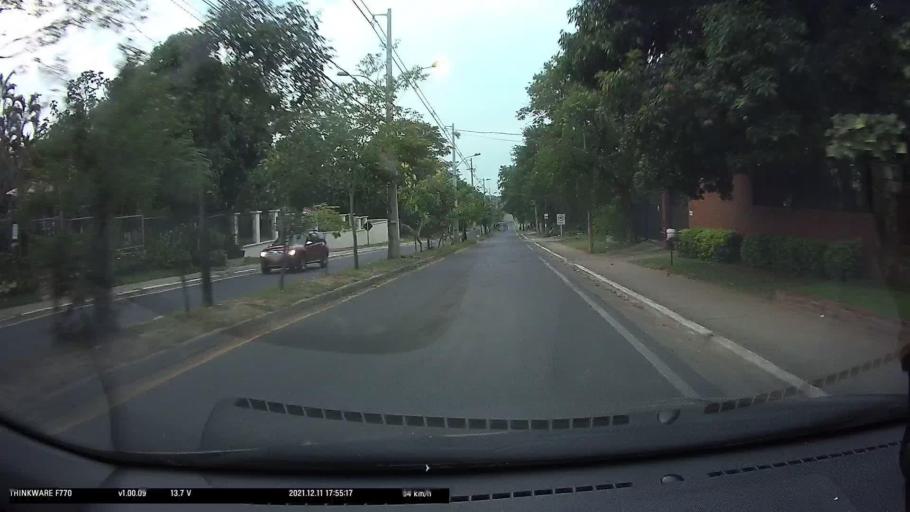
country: PY
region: Cordillera
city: San Bernardino
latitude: -25.3019
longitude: -57.3006
